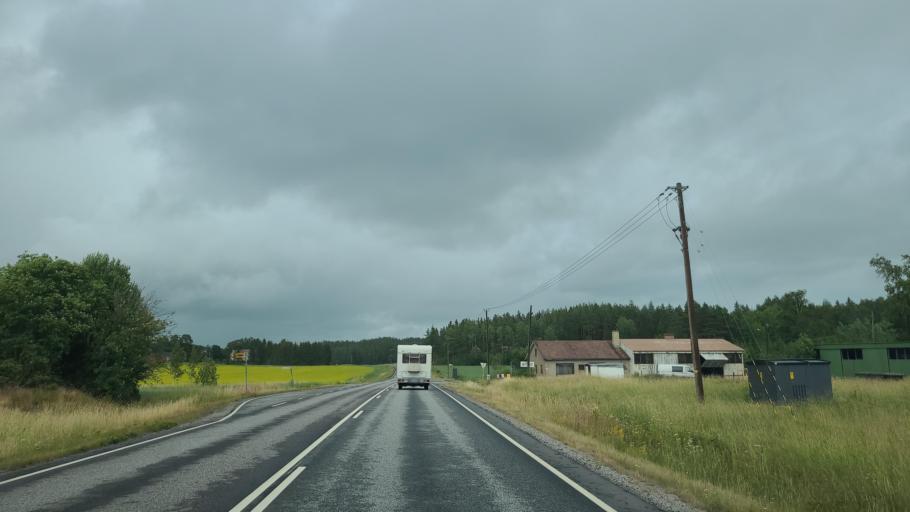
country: FI
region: Varsinais-Suomi
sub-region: Turku
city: Sauvo
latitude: 60.2577
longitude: 22.6322
